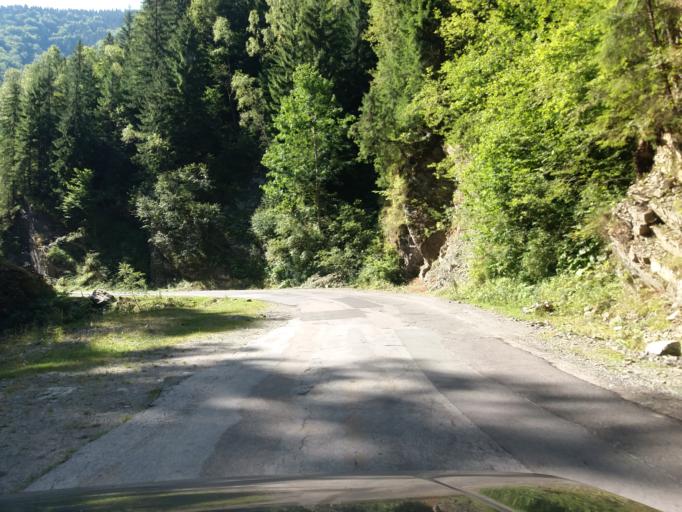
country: RO
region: Hunedoara
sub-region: Oras Petrila
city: Petrila
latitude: 45.4126
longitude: 23.4734
